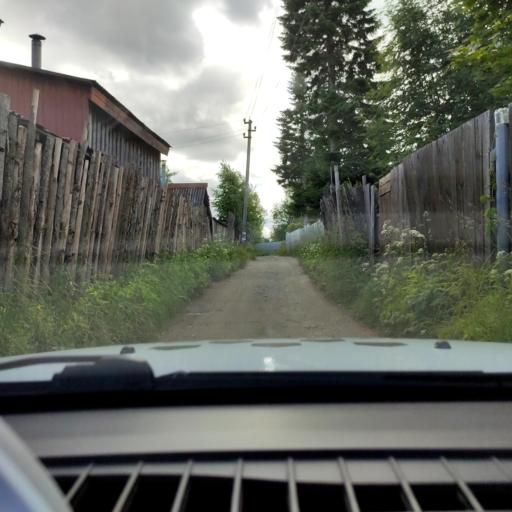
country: RU
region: Perm
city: Overyata
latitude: 58.1013
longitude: 55.8625
